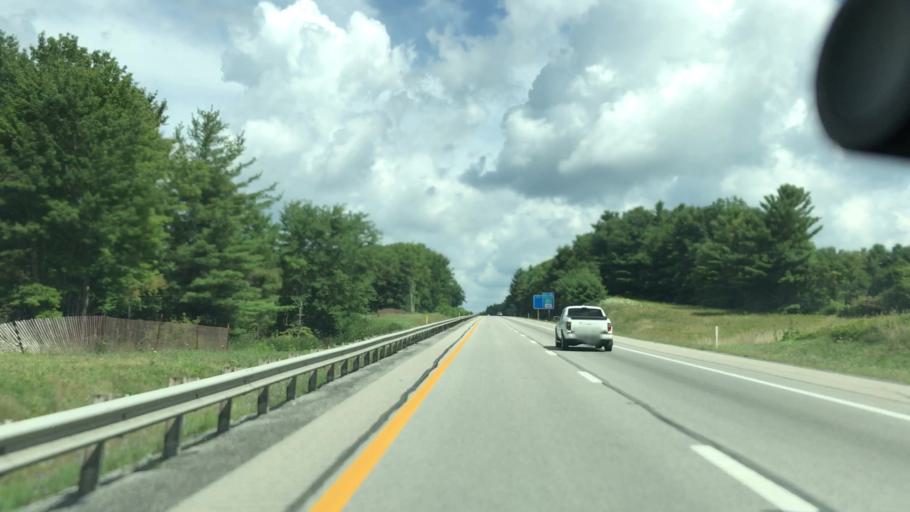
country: US
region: West Virginia
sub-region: Mercer County
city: Athens
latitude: 37.4076
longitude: -81.0608
